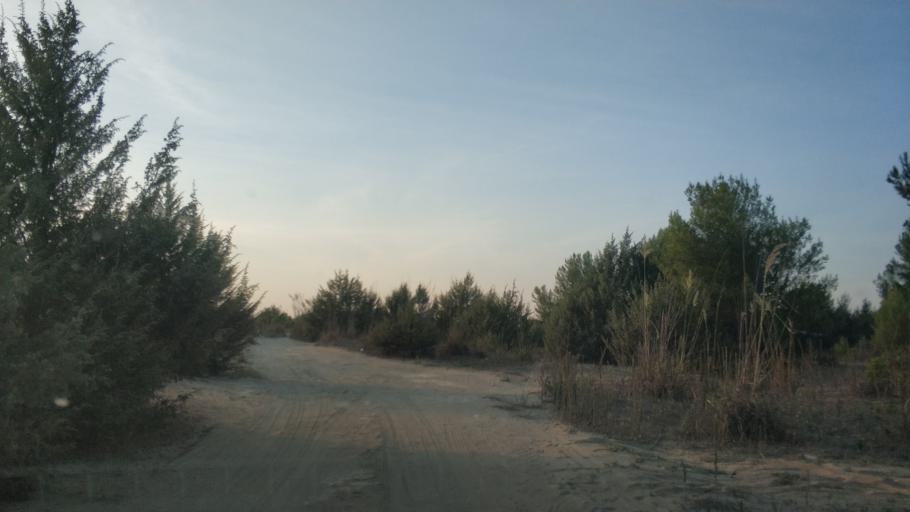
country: AL
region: Fier
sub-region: Rrethi i Lushnjes
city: Divjake
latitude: 40.9536
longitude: 19.4733
